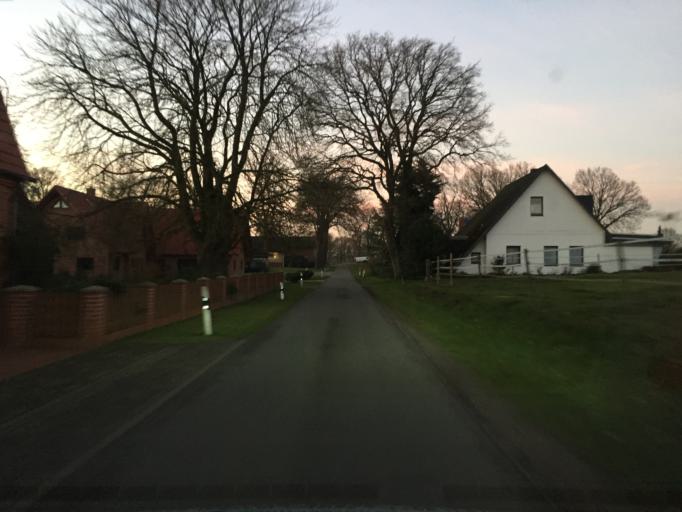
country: DE
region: Lower Saxony
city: Hassel
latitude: 52.6672
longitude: 8.8360
